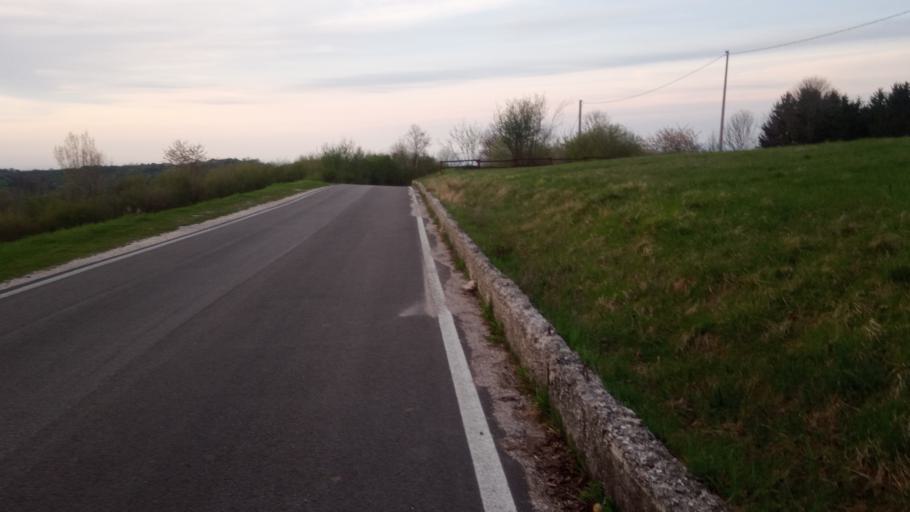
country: IT
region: Veneto
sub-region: Provincia di Vicenza
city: Conco
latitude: 45.8014
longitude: 11.6240
